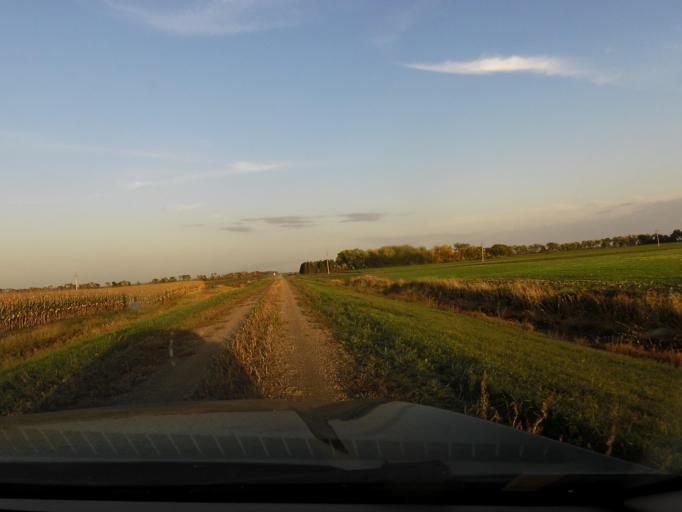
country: US
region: North Dakota
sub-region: Walsh County
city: Grafton
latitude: 48.3975
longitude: -97.2357
